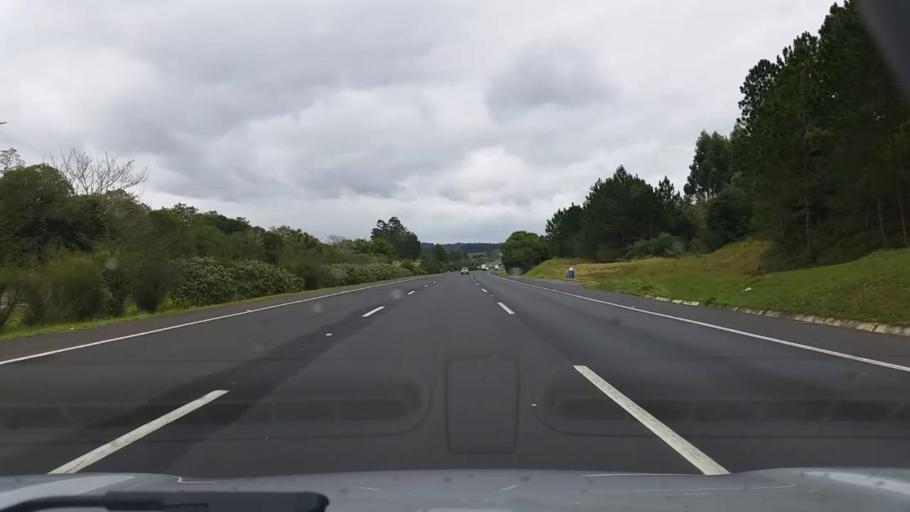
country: BR
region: Rio Grande do Sul
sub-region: Gravatai
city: Gravatai
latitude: -29.9194
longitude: -50.8308
